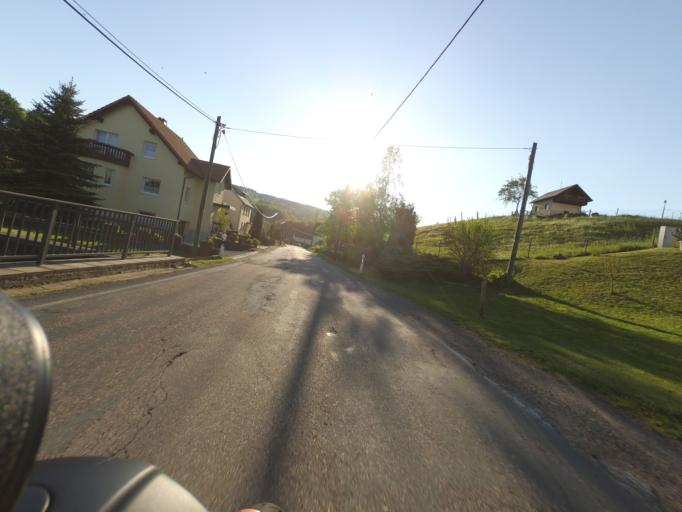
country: DE
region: Saxony
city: Glashutte
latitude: 50.8355
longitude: 13.7425
